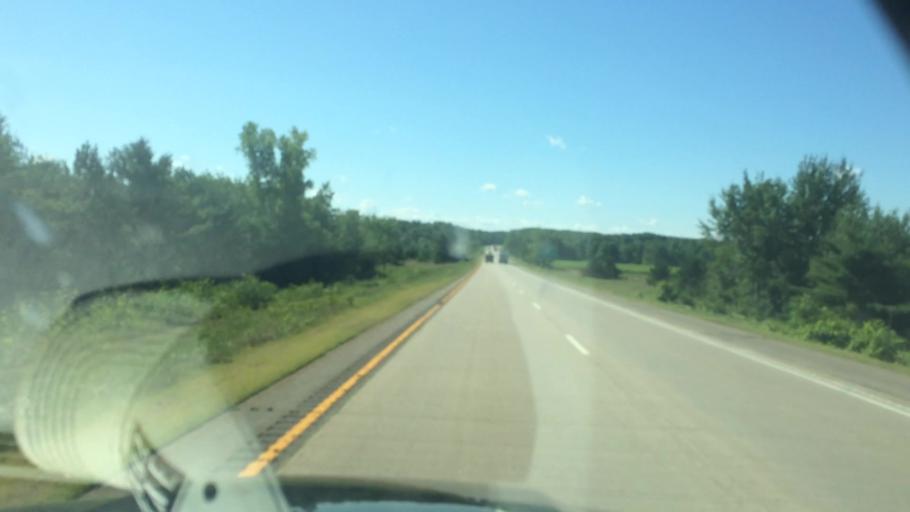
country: US
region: Wisconsin
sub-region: Marathon County
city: Mosinee
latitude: 44.6985
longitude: -89.6493
